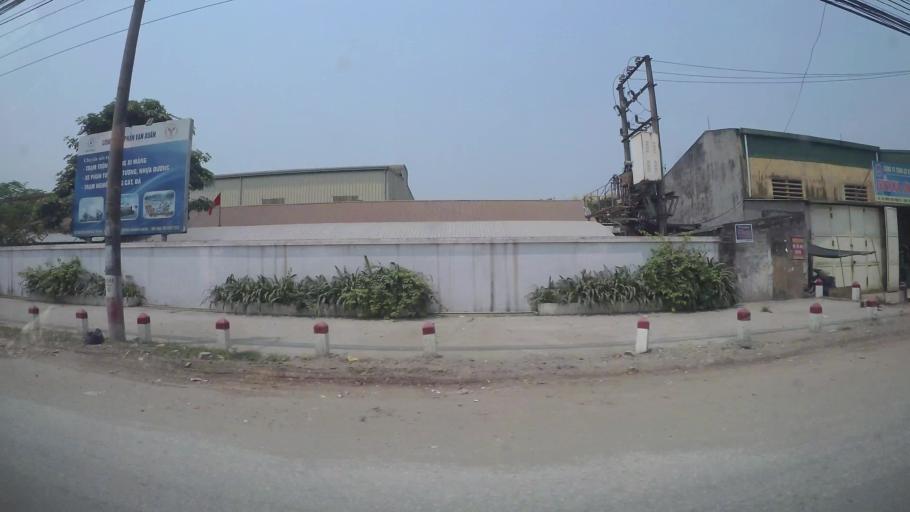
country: VN
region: Ha Noi
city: Van Dien
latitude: 20.9438
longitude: 105.8388
